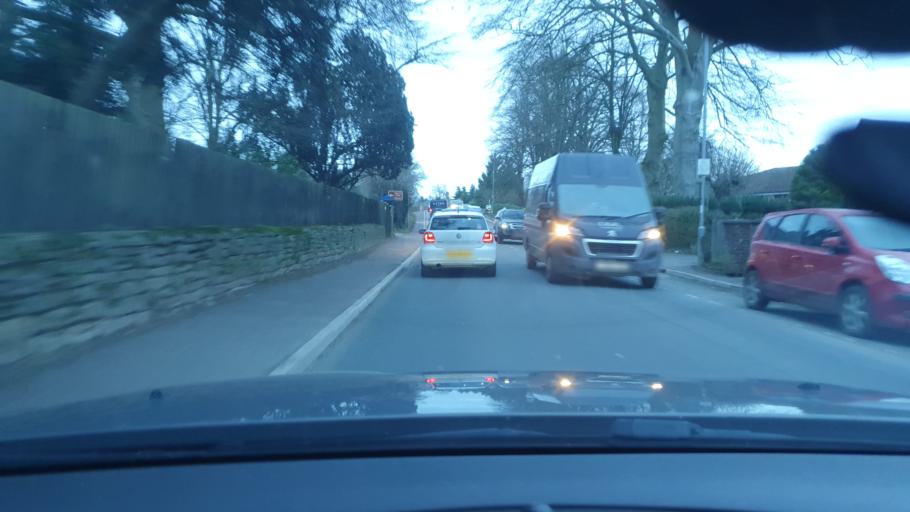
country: GB
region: England
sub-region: Wiltshire
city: Devizes
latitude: 51.3534
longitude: -1.9853
